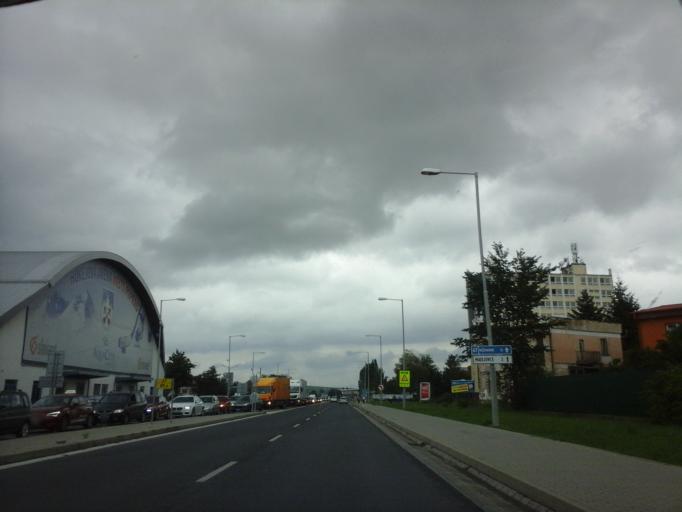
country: SK
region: Presovsky
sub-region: Okres Poprad
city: Poprad
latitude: 49.0596
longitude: 20.3108
